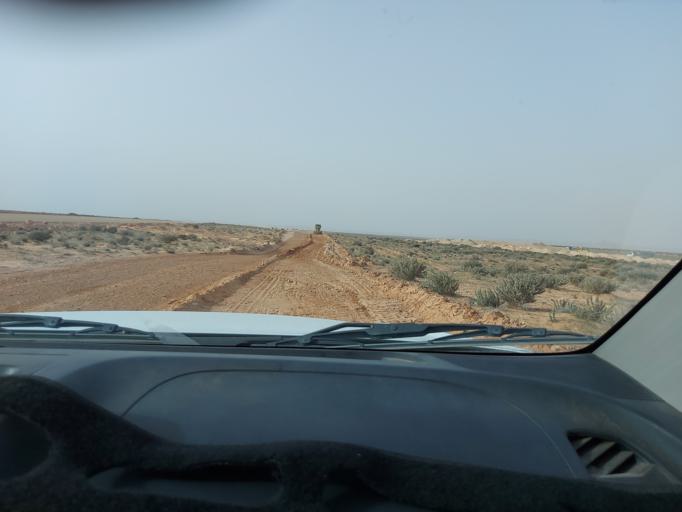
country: TN
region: Madanin
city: Medenine
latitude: 33.2622
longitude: 10.5773
